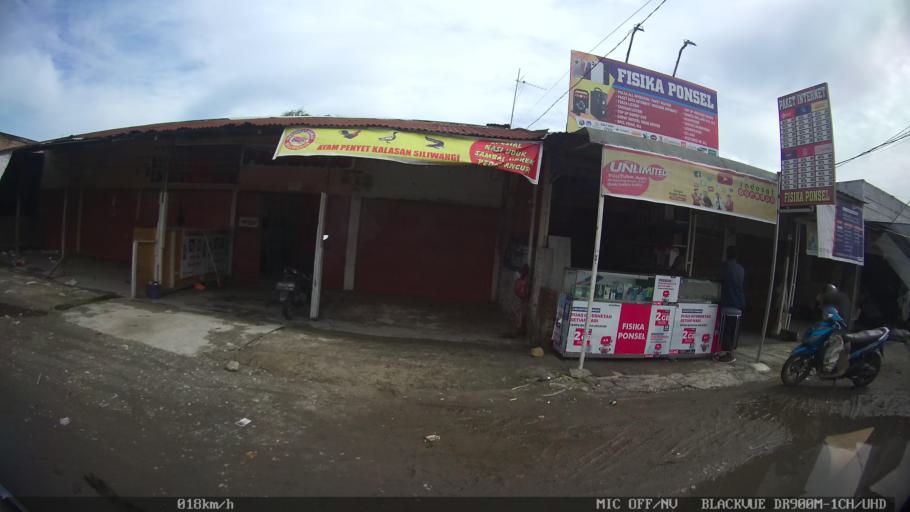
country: ID
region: North Sumatra
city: Medan
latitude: 3.6207
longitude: 98.7289
